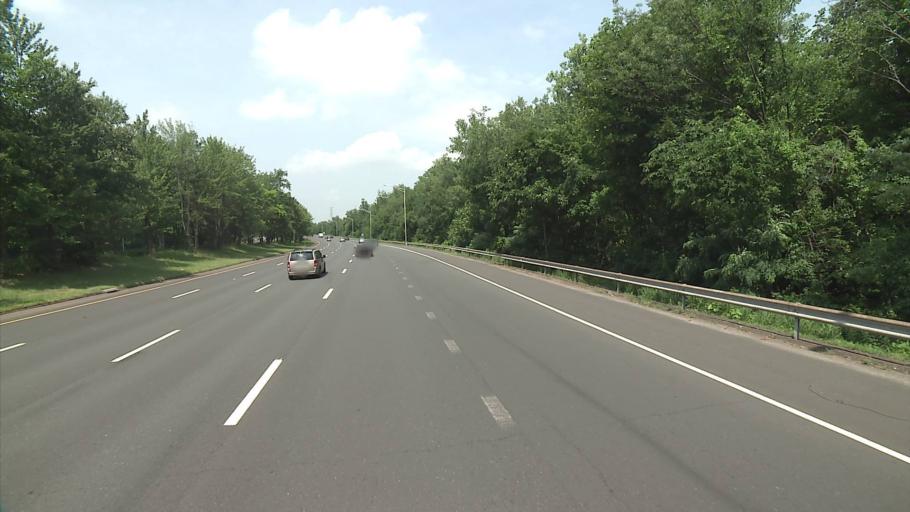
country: US
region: Connecticut
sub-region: Hartford County
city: Manchester
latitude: 41.7645
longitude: -72.5459
